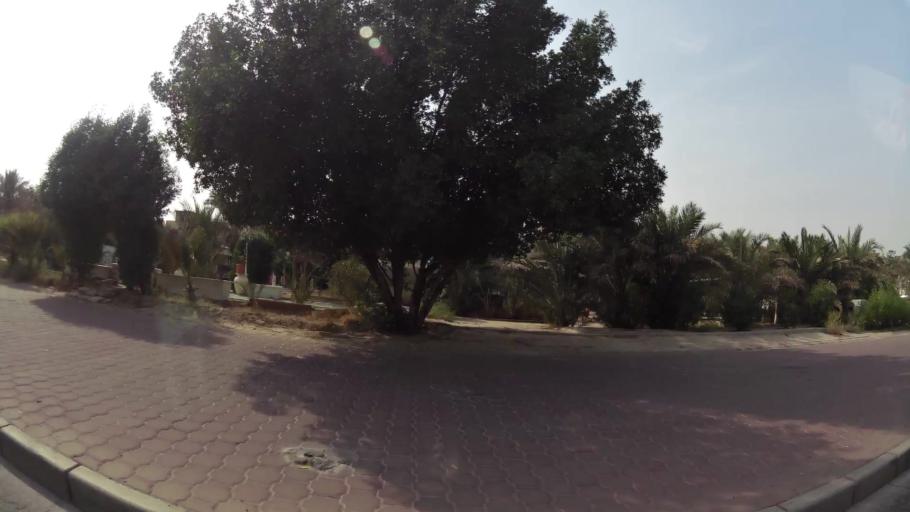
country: KW
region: Al Asimah
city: Ar Rabiyah
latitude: 29.2928
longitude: 47.9392
